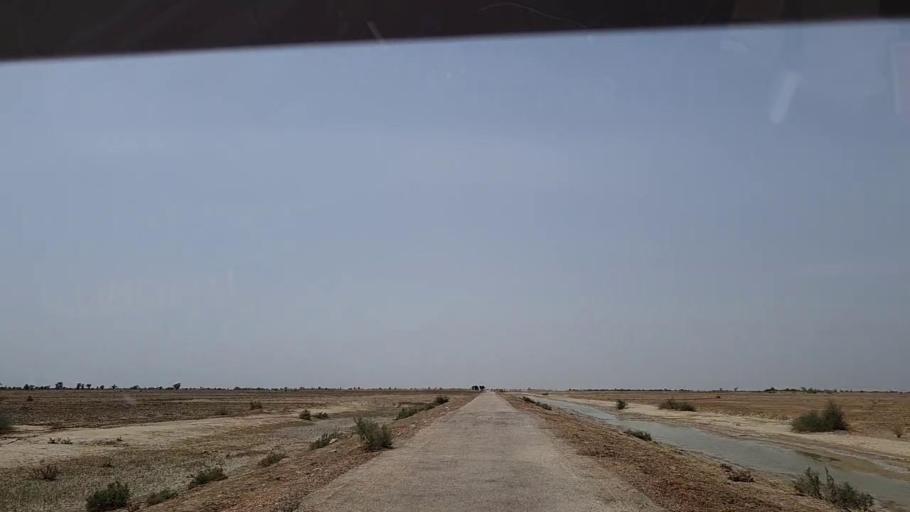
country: PK
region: Sindh
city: Johi
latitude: 26.7251
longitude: 67.6421
